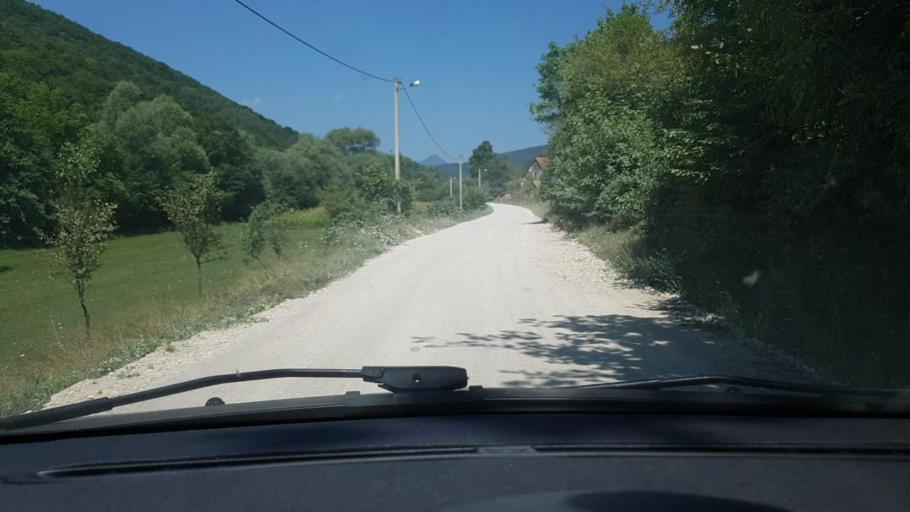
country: BA
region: Federation of Bosnia and Herzegovina
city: Orasac
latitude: 44.5404
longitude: 16.1103
